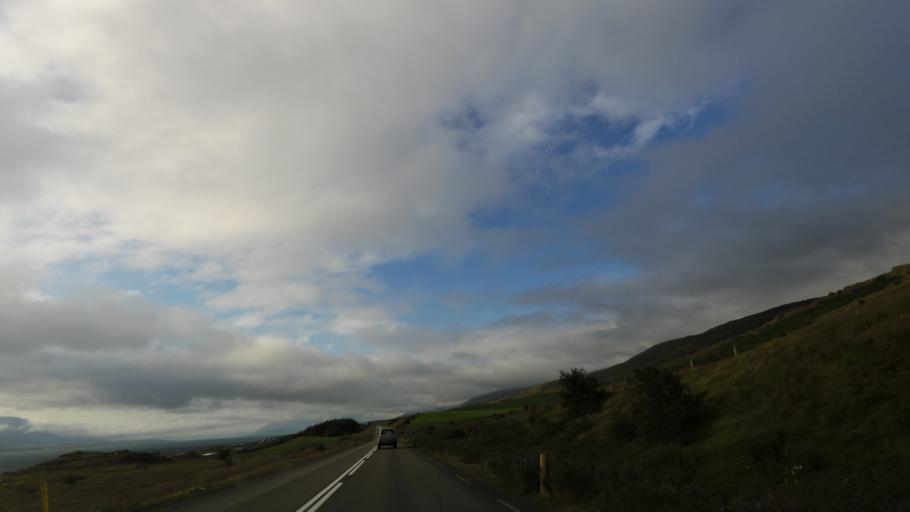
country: IS
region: Northeast
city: Akureyri
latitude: 65.7271
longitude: -18.0738
